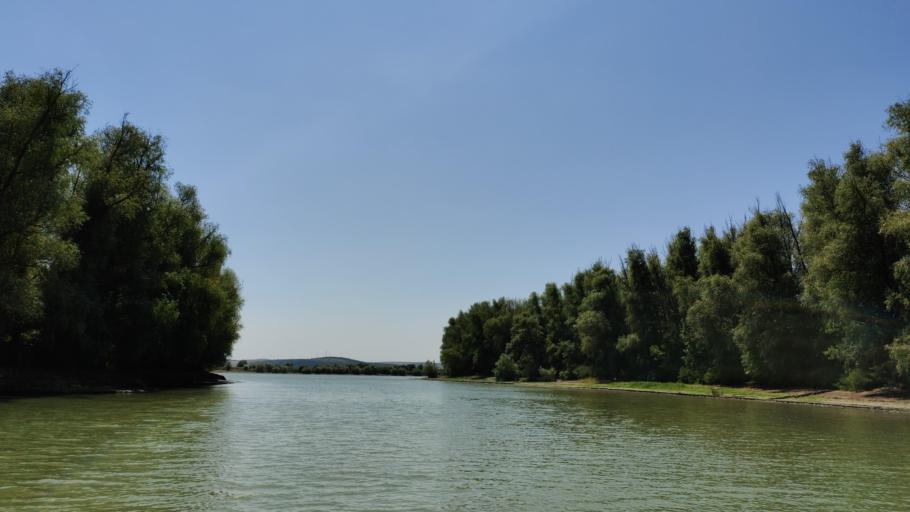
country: RO
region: Tulcea
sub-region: Municipiul Tulcea
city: Tulcea
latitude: 45.2066
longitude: 28.8536
